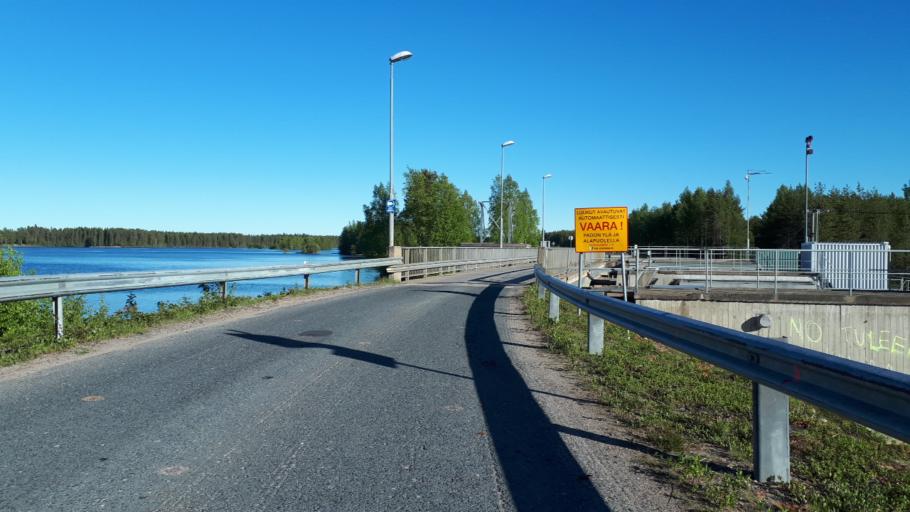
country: FI
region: Northern Ostrobothnia
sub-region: Oulunkaari
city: Ii
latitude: 65.3253
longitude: 25.5239
